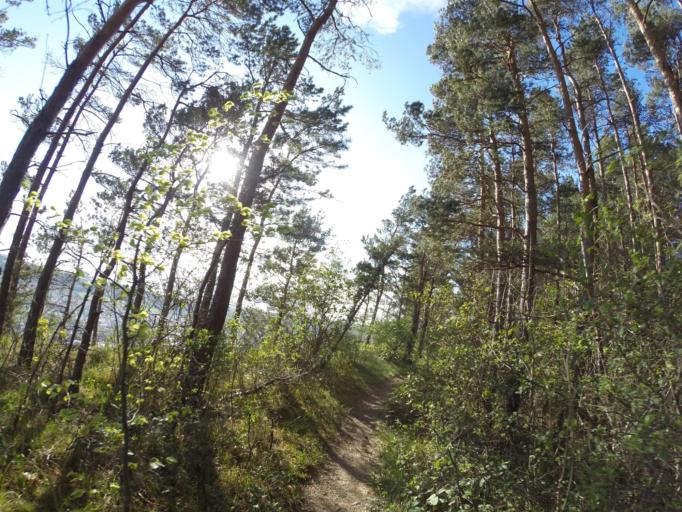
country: DE
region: Thuringia
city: Jena
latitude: 50.9013
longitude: 11.6082
